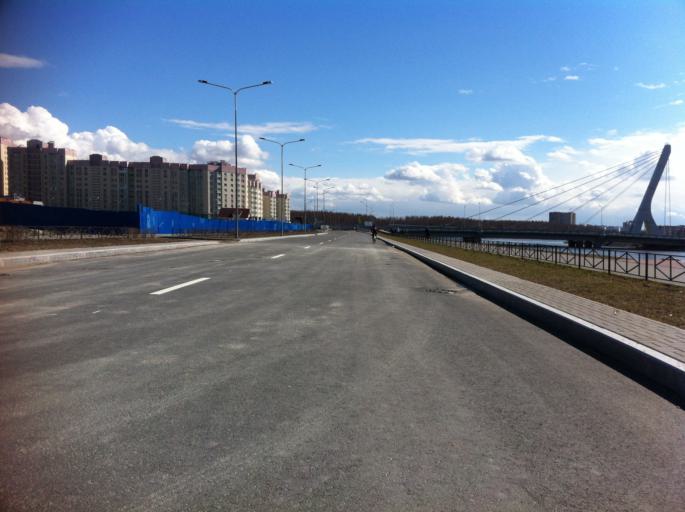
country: RU
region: St.-Petersburg
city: Sosnovaya Polyana
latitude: 59.8616
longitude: 30.1544
